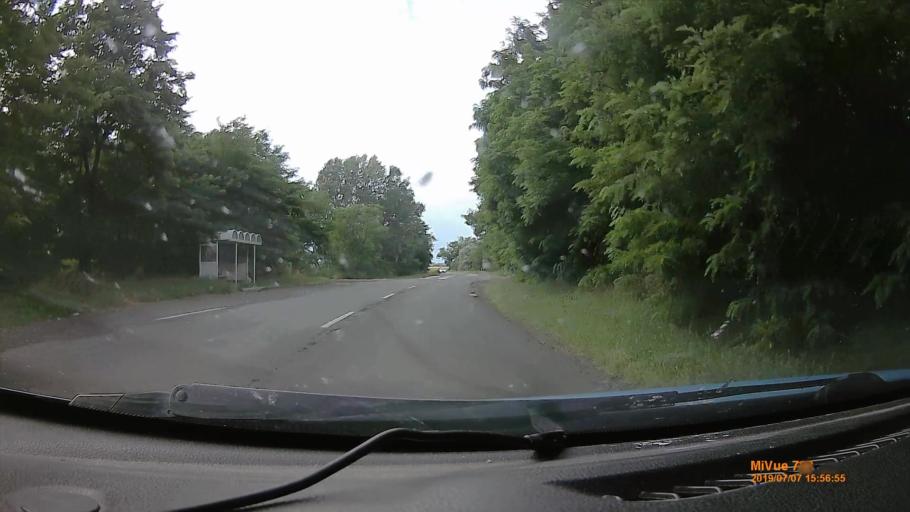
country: HU
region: Pest
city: Szentlorinckata
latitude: 47.5725
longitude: 19.7682
